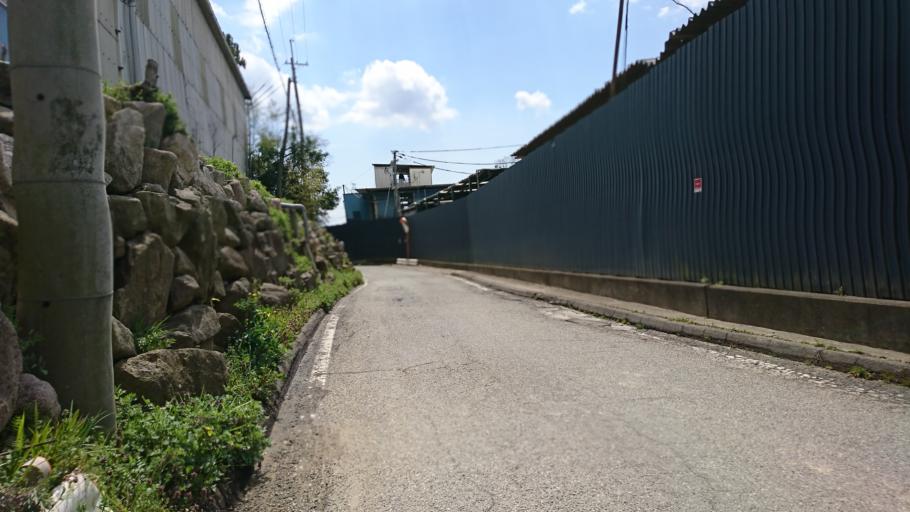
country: JP
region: Hyogo
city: Miki
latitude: 34.7710
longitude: 134.9611
